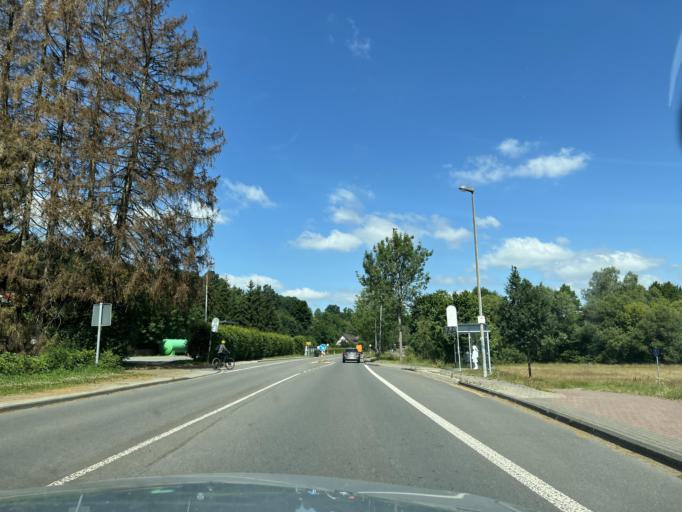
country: DE
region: North Rhine-Westphalia
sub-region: Regierungsbezirk Arnsberg
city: Wenden
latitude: 50.9546
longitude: 7.8213
